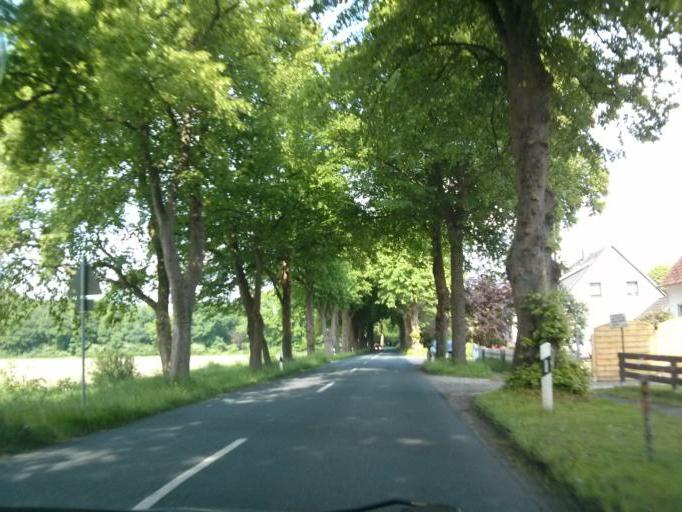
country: DE
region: Lower Saxony
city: Loxstedt
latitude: 53.4770
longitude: 8.6682
